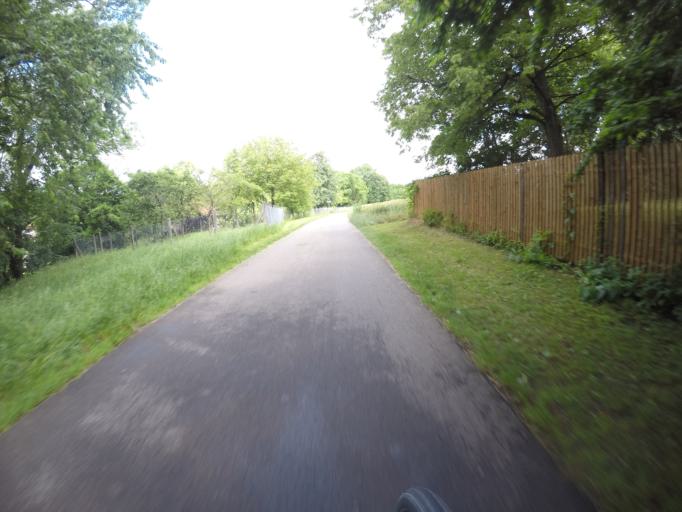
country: DE
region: Baden-Wuerttemberg
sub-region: Regierungsbezirk Stuttgart
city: Kuchen
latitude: 48.6458
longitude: 9.7972
